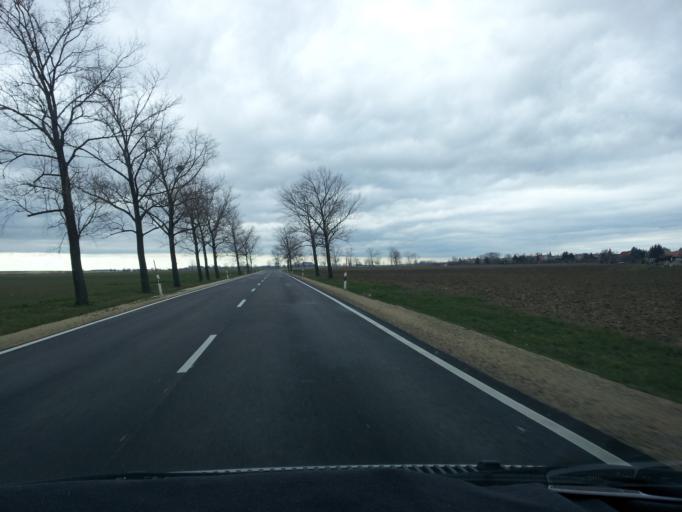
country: HU
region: Gyor-Moson-Sopron
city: Beled
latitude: 47.4624
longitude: 17.1088
